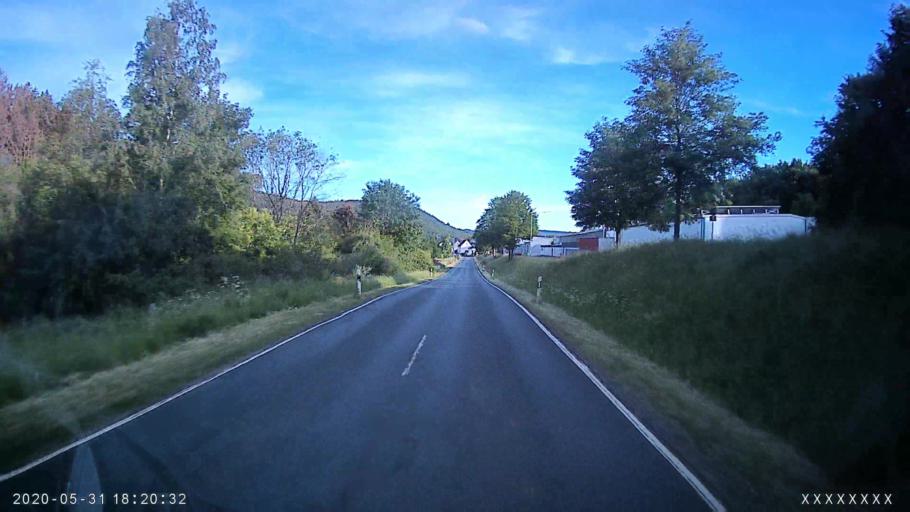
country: DE
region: Hesse
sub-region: Regierungsbezirk Giessen
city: Haiger
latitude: 50.7774
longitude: 8.2068
